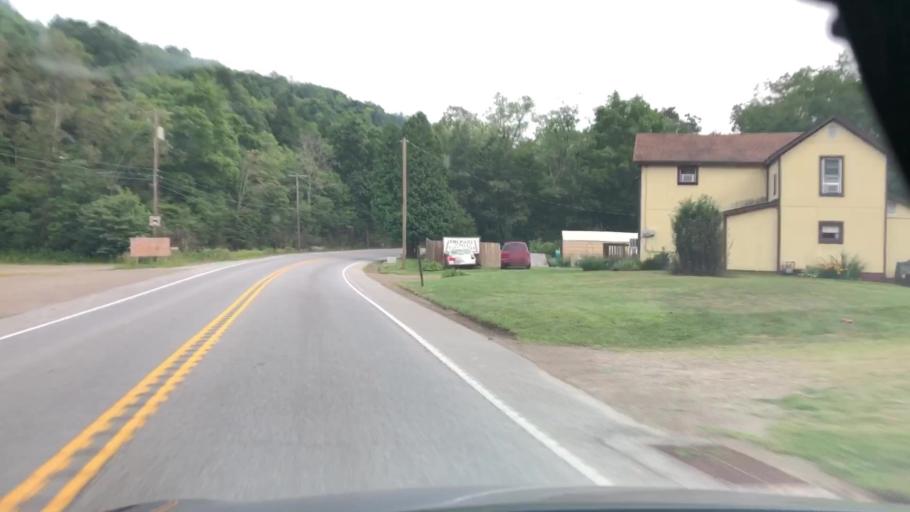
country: US
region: Pennsylvania
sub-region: Venango County
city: Hasson Heights
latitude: 41.4971
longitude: -79.7009
